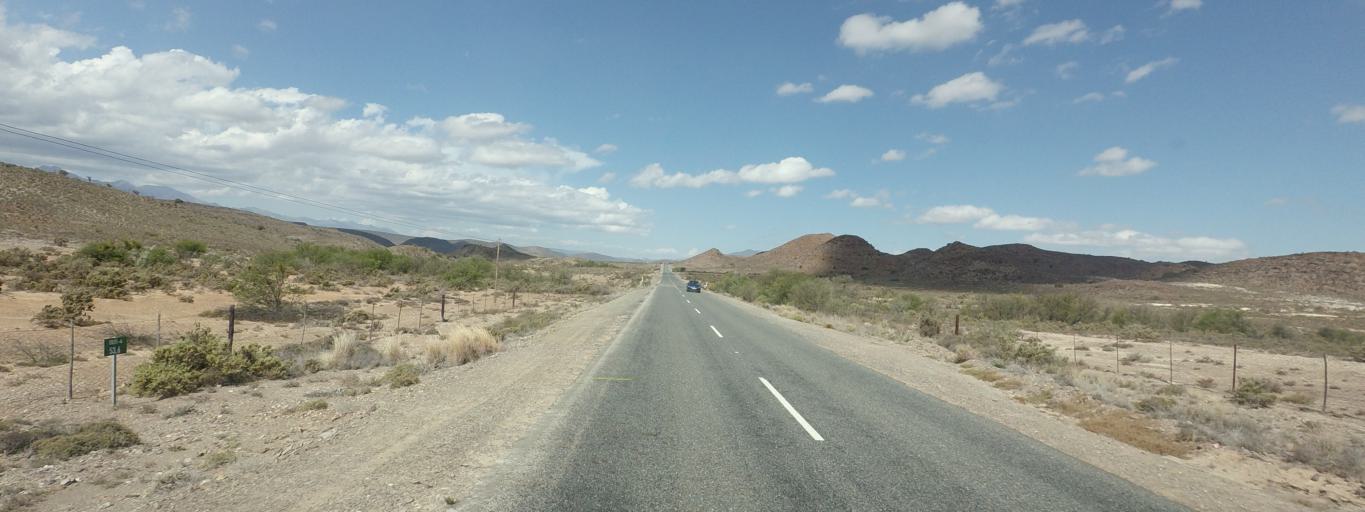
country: ZA
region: Western Cape
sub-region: Eden District Municipality
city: Ladismith
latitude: -33.5996
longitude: 21.1044
